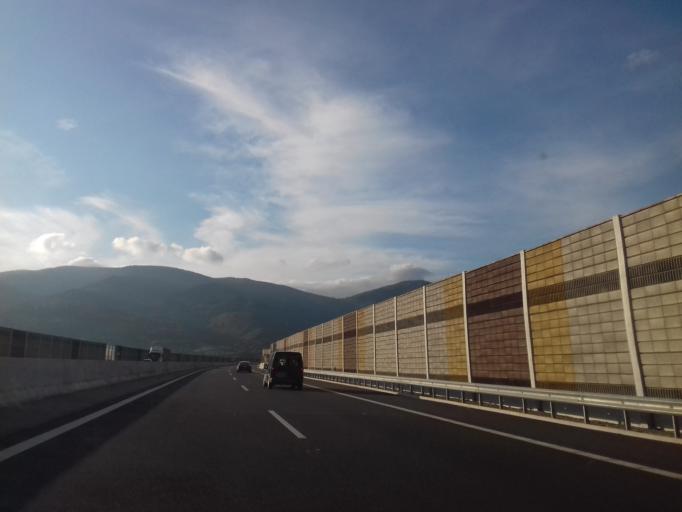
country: SK
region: Zilinsky
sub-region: Okres Zilina
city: Vrutky
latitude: 49.1226
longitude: 18.9260
